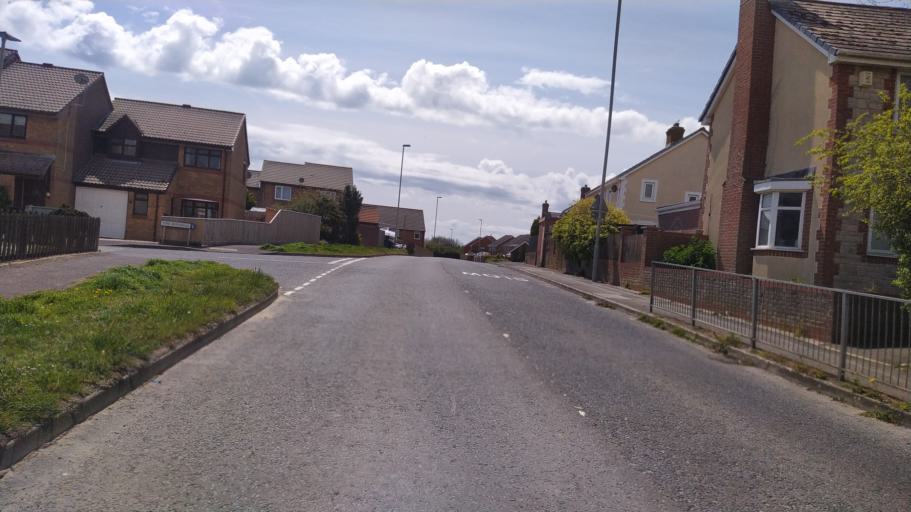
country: GB
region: England
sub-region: Dorset
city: Chickerell
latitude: 50.6209
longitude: -2.4975
